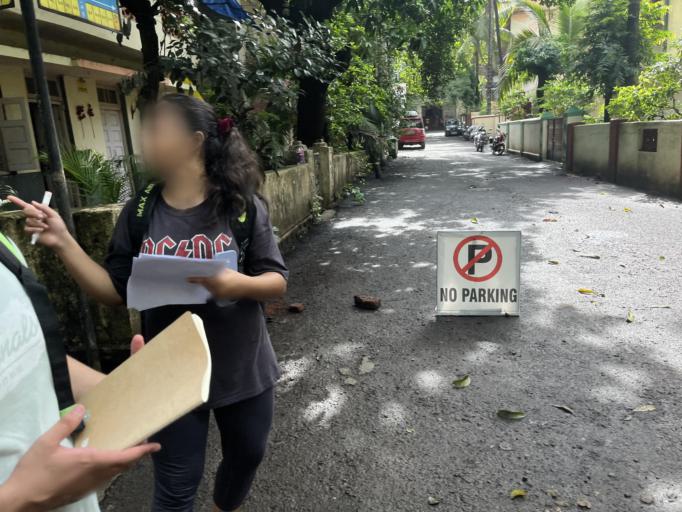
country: IN
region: Maharashtra
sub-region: Mumbai Suburban
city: Borivli
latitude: 19.2331
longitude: 72.8657
